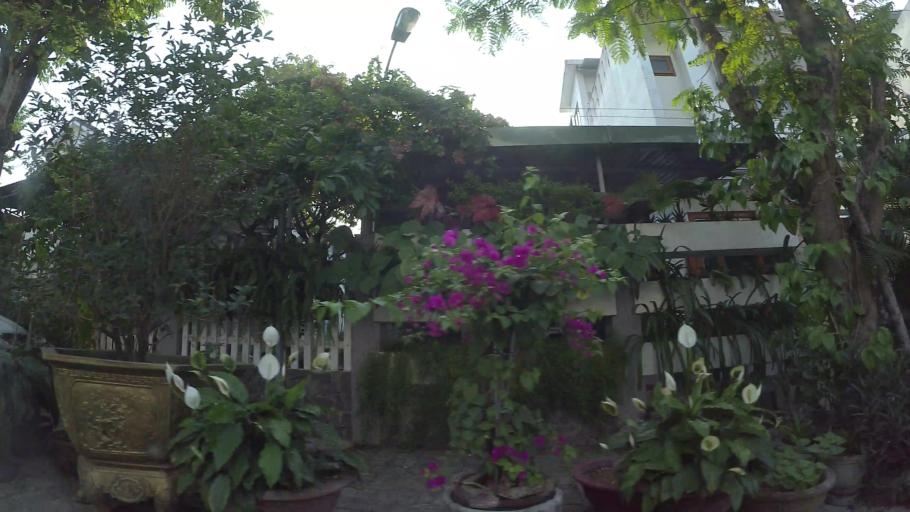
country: VN
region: Da Nang
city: Cam Le
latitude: 16.0202
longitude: 108.2061
